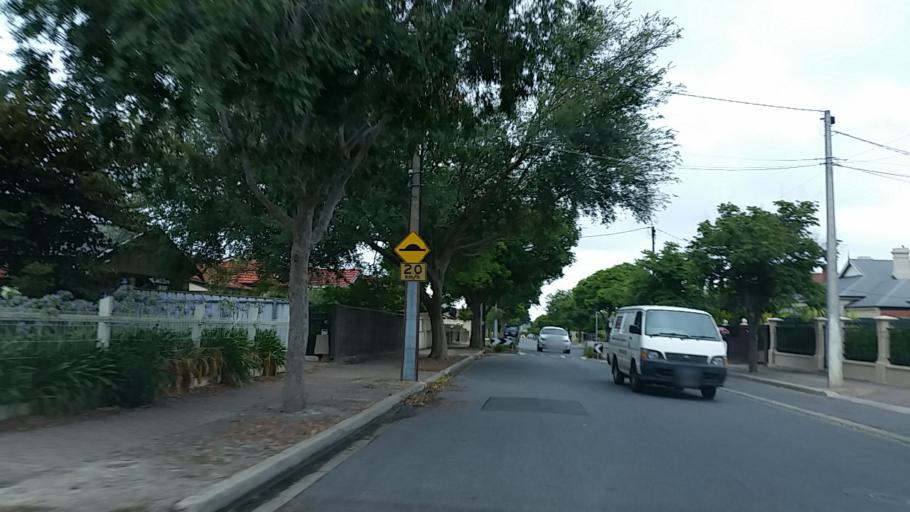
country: AU
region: South Australia
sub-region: Prospect
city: Prospect
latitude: -34.8780
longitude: 138.5990
